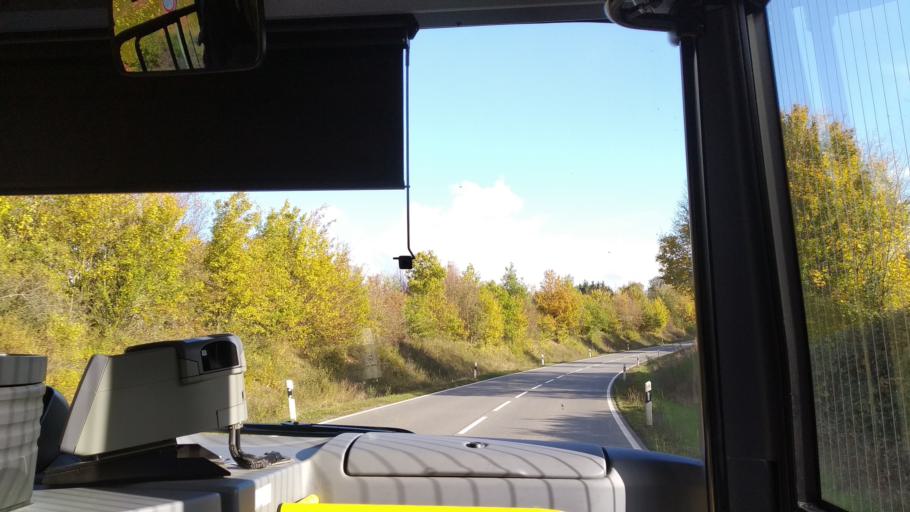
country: DE
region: Rheinland-Pfalz
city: Diez
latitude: 50.3629
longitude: 8.0126
